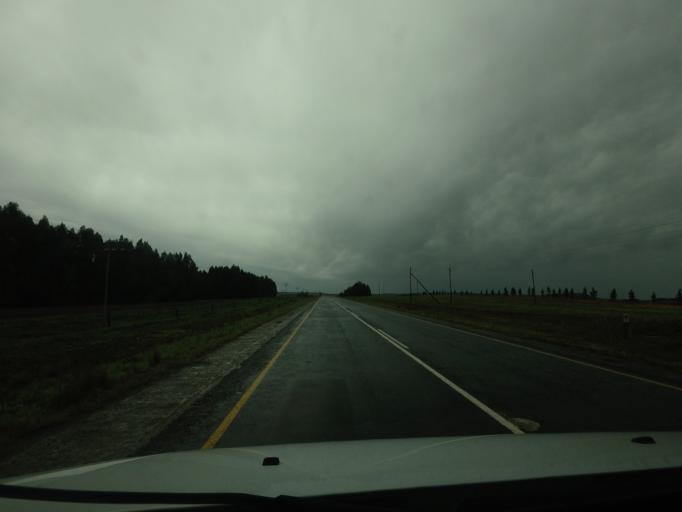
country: ZA
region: Mpumalanga
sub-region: Nkangala District Municipality
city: Belfast
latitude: -25.4868
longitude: 30.0916
